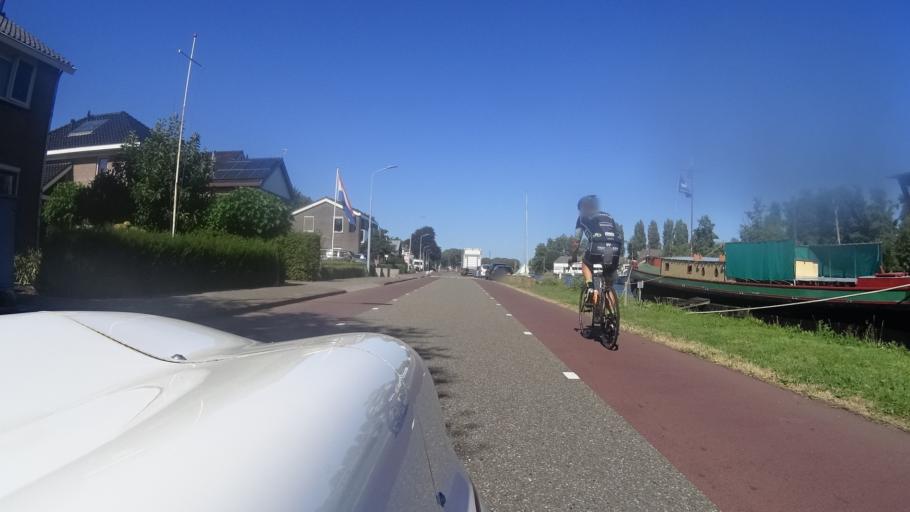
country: NL
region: South Holland
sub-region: Gemeente Kaag en Braassem
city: Oude Wetering
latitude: 52.2229
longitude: 4.6500
